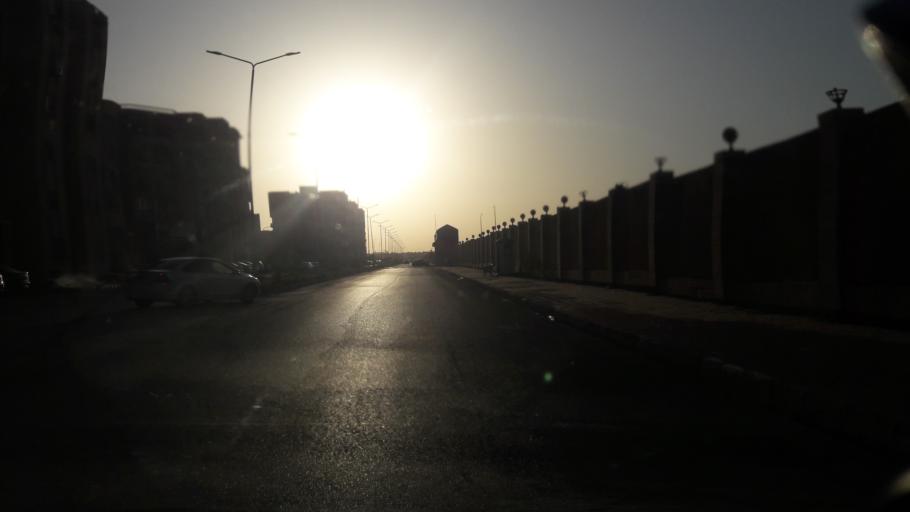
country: EG
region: Al Jizah
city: Madinat Sittah Uktubar
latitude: 29.9585
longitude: 31.0428
